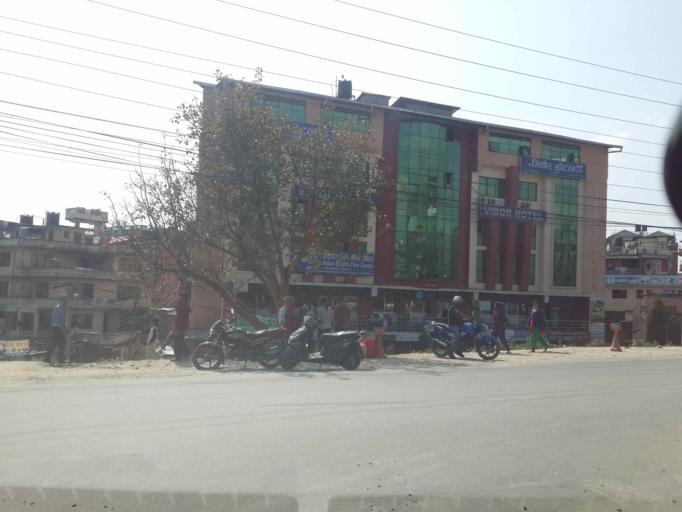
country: NP
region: Central Region
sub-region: Bagmati Zone
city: Kathmandu
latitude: 27.7319
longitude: 85.3443
